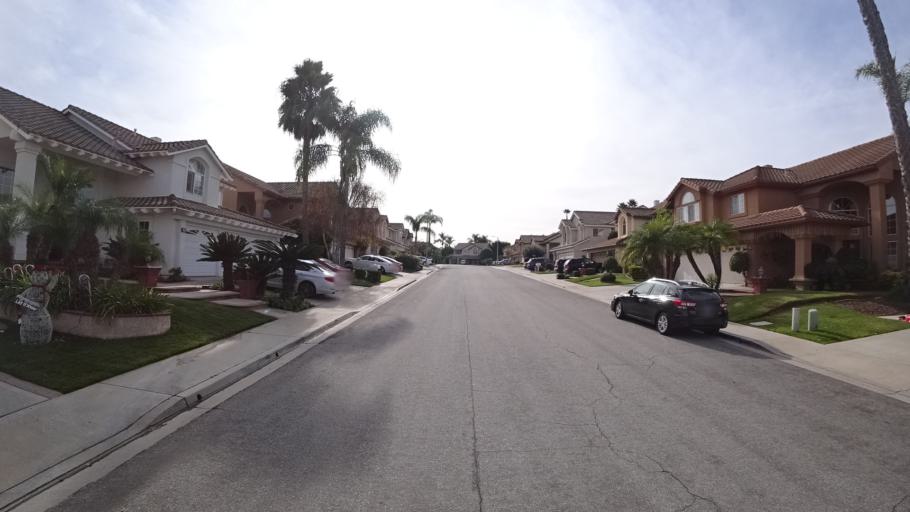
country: US
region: California
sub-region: Orange County
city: Laguna Woods
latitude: 33.5919
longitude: -117.7340
